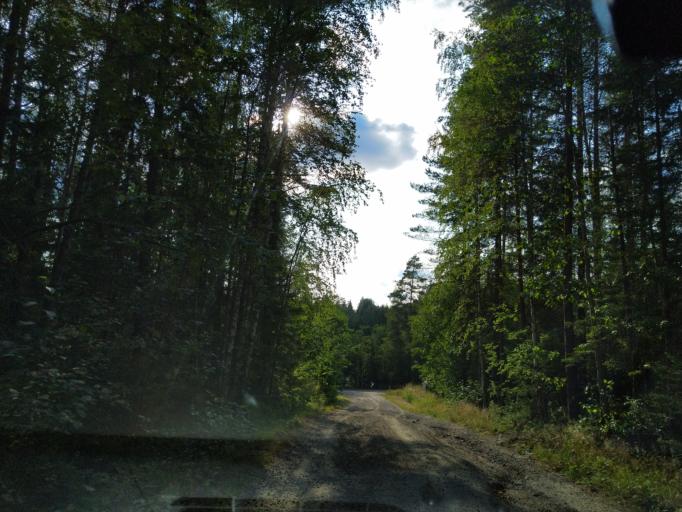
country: FI
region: Central Finland
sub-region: Jaemsae
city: Kuhmoinen
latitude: 61.7147
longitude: 24.9112
